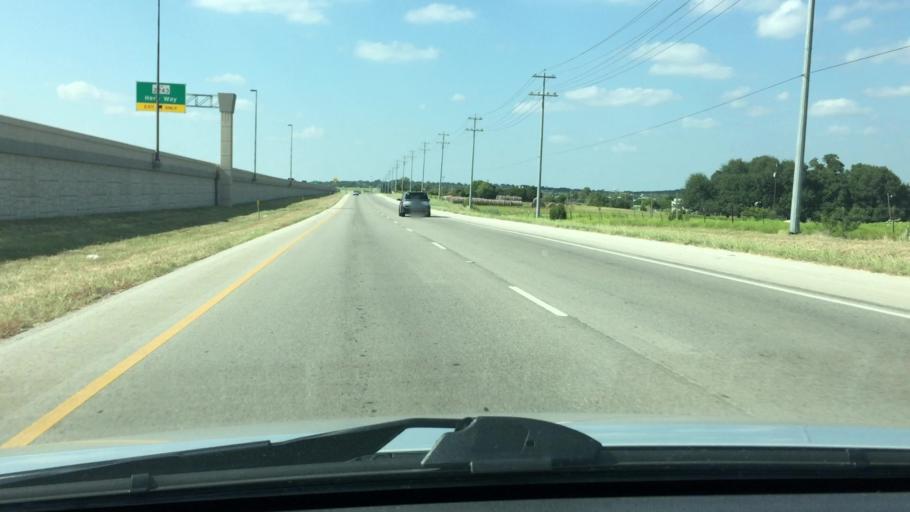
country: US
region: Texas
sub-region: Williamson County
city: Leander
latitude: 30.5747
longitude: -97.8310
